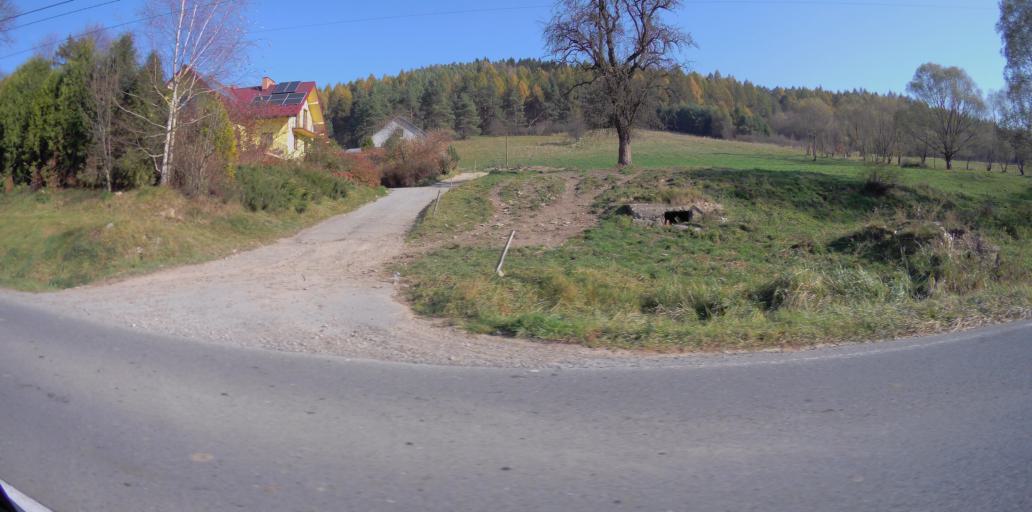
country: PL
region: Subcarpathian Voivodeship
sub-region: Powiat bieszczadzki
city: Ustrzyki Dolne
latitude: 49.4828
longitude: 22.6643
